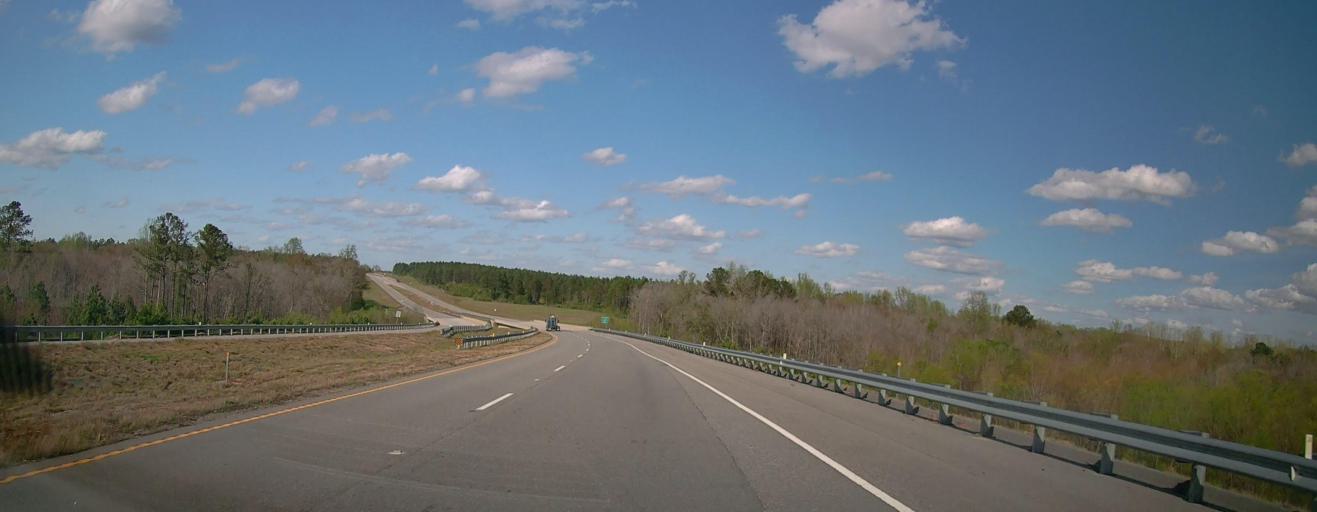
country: US
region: Georgia
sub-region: Baldwin County
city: Hardwick
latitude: 32.9822
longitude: -83.2073
